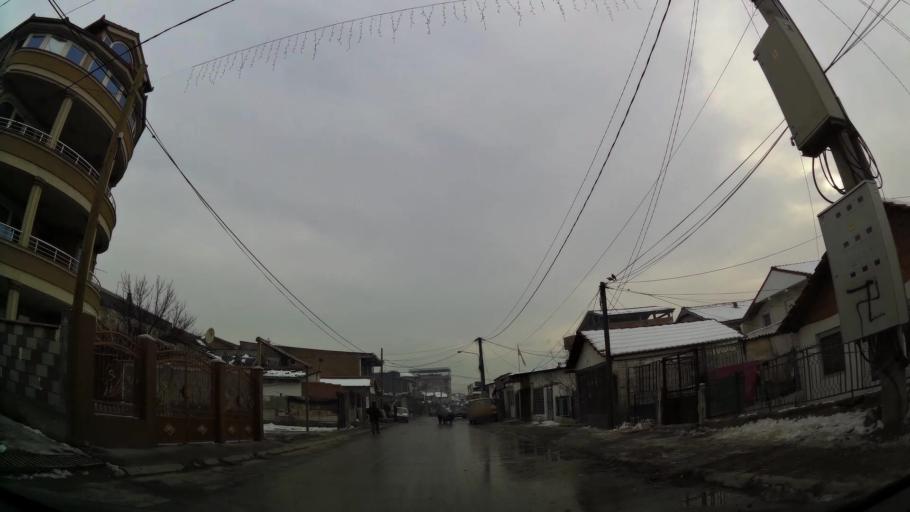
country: MK
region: Suto Orizari
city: Suto Orizare
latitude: 42.0436
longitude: 21.4232
